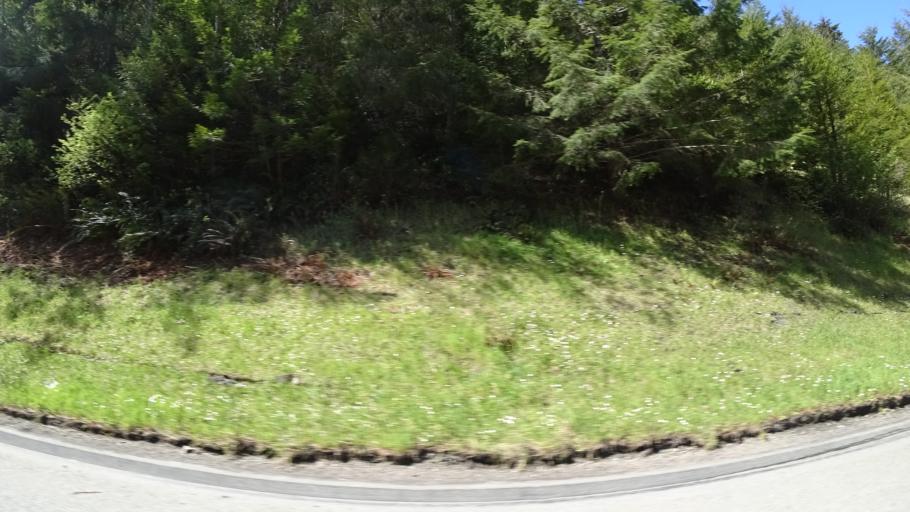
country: US
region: California
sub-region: Del Norte County
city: Bertsch-Oceanview
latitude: 41.4300
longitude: -124.0175
